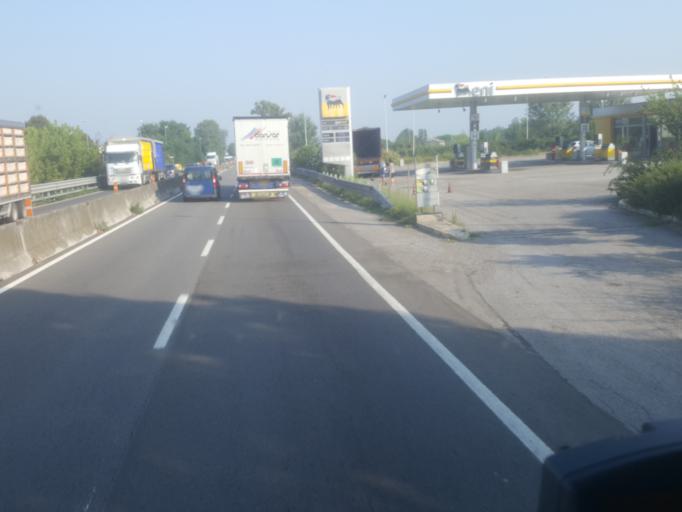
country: IT
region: Emilia-Romagna
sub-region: Provincia di Ravenna
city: Ravenna
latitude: 44.4146
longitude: 12.1700
